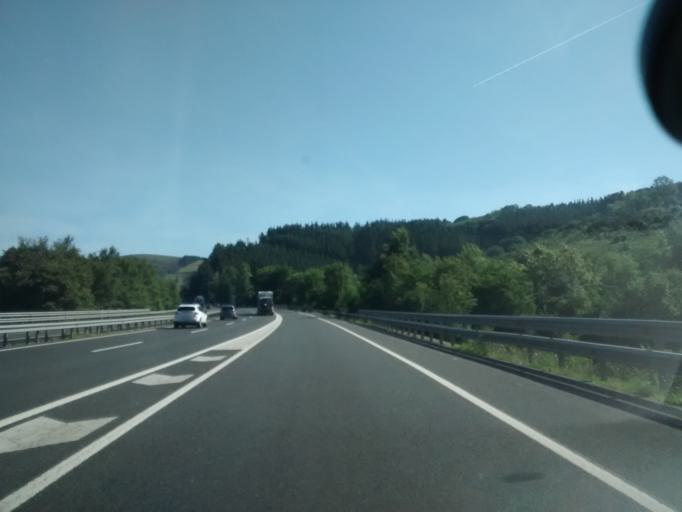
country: ES
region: Basque Country
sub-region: Provincia de Guipuzcoa
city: Cestona
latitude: 43.2650
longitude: -2.2729
